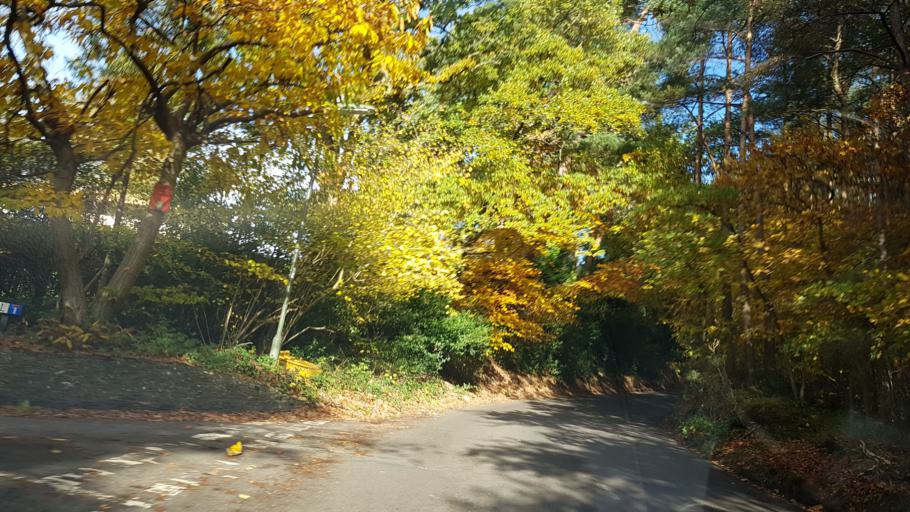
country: GB
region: England
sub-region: Surrey
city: Seale
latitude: 51.2047
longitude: -0.7518
